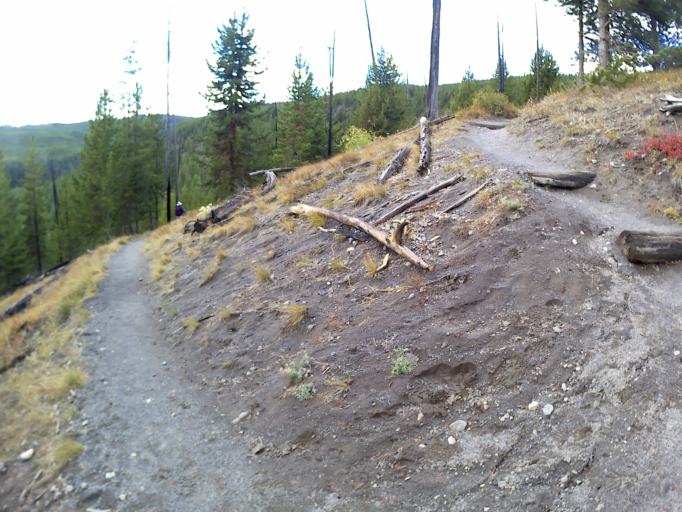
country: US
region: Montana
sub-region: Gallatin County
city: West Yellowstone
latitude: 44.4857
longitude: -110.8746
